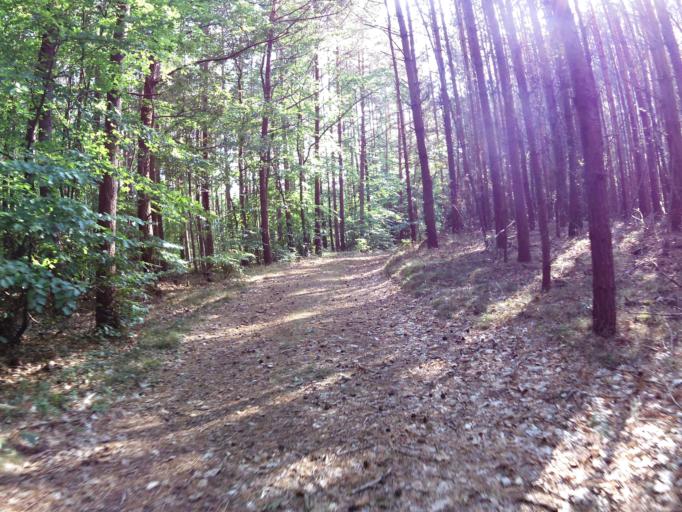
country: DE
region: Mecklenburg-Vorpommern
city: Loddin
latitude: 54.0079
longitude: 14.0552
